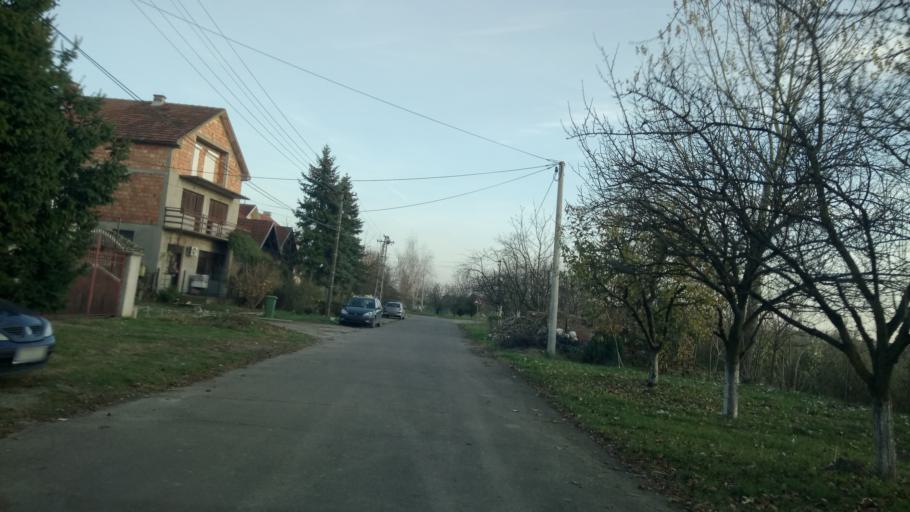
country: RS
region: Autonomna Pokrajina Vojvodina
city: Nova Pazova
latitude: 44.9334
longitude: 20.2178
